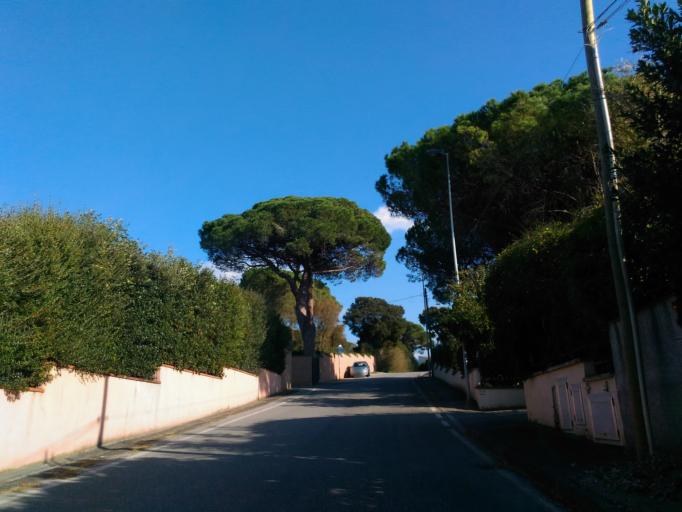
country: IT
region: Tuscany
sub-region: Provincia di Livorno
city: Livorno
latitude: 43.5105
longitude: 10.3392
